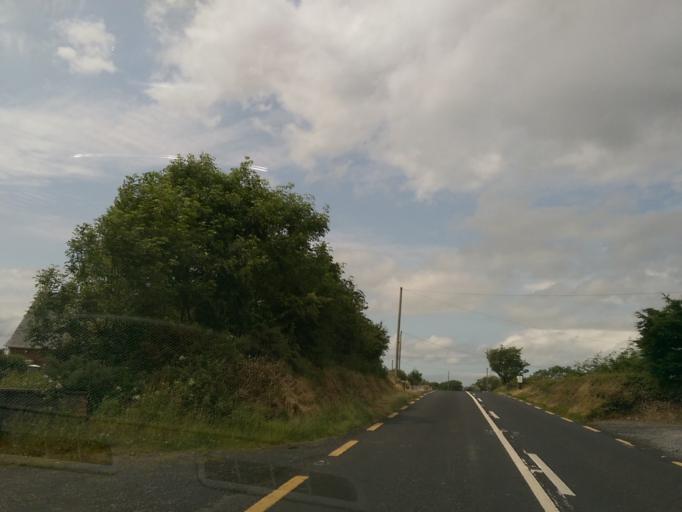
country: IE
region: Munster
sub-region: An Clar
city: Kilrush
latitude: 52.6471
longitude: -9.5002
